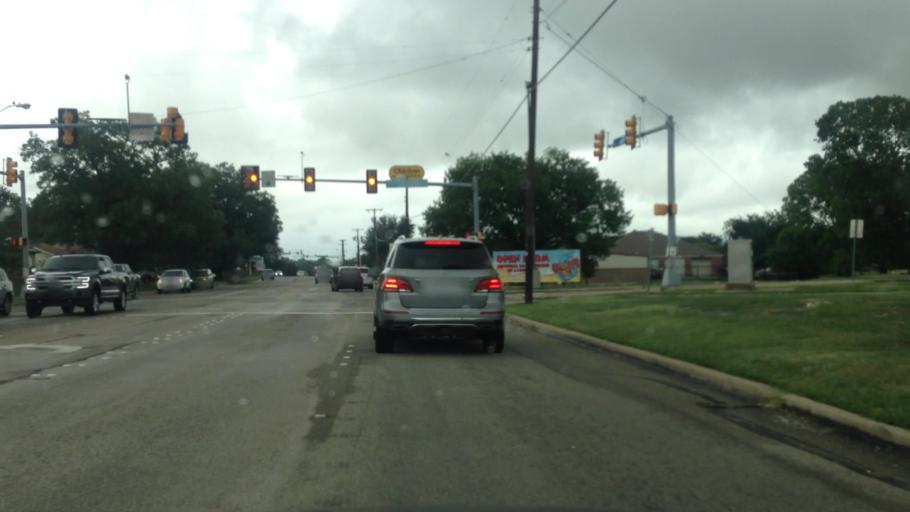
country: US
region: Texas
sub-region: Tarrant County
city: White Settlement
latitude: 32.7661
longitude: -97.4720
